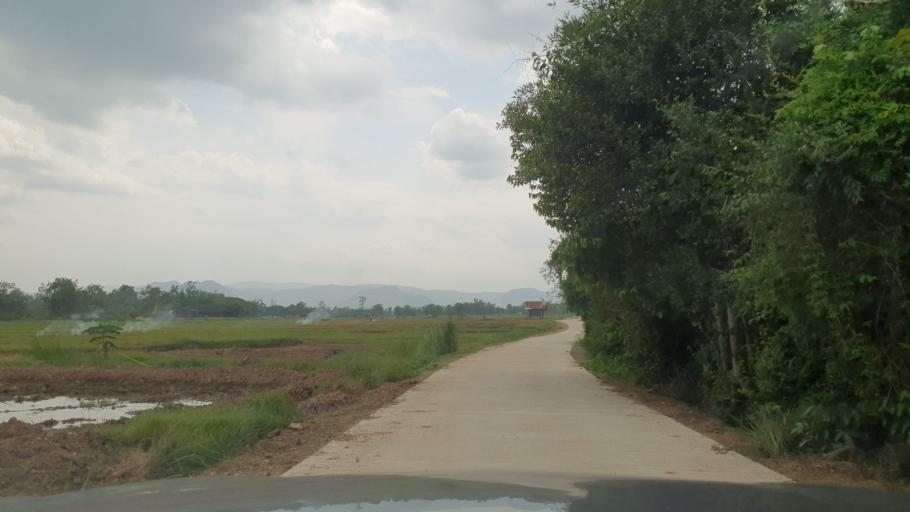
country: TH
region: Sukhothai
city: Thung Saliam
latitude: 17.3294
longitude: 99.4495
